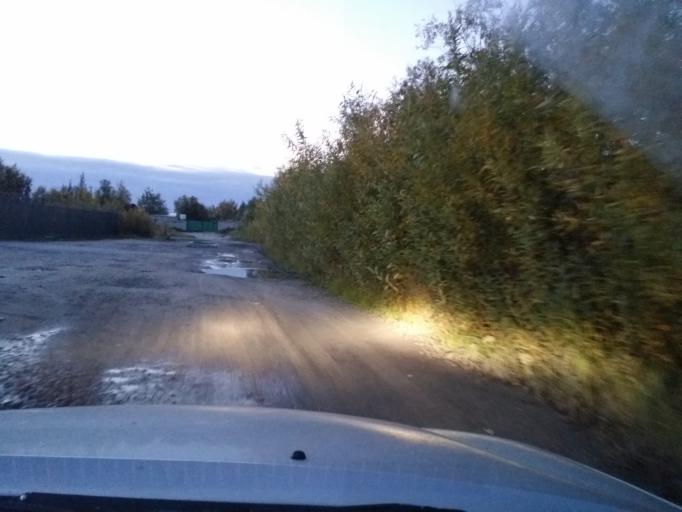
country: RU
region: Khanty-Mansiyskiy Avtonomnyy Okrug
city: Nizhnevartovsk
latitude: 60.9596
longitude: 76.5280
